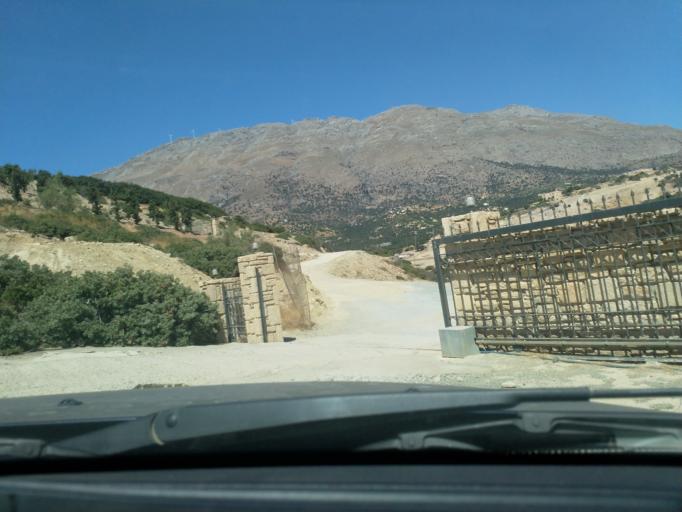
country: GR
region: Crete
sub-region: Nomos Rethymnis
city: Agia Galini
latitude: 35.1187
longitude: 24.5572
